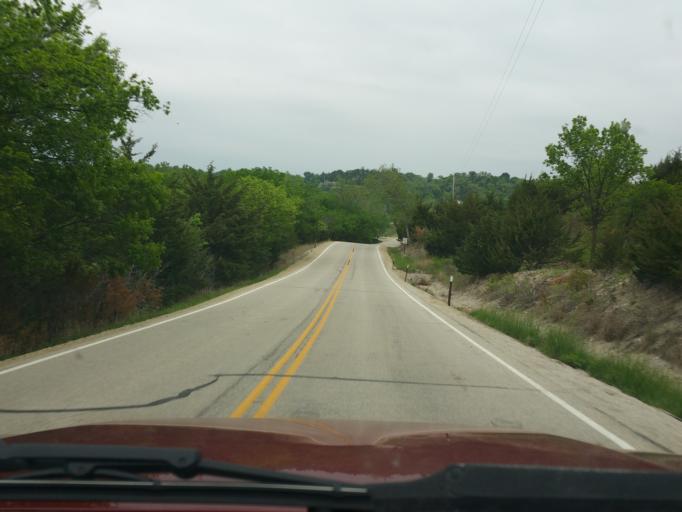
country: US
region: Kansas
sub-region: Riley County
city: Manhattan
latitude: 39.2756
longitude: -96.6298
